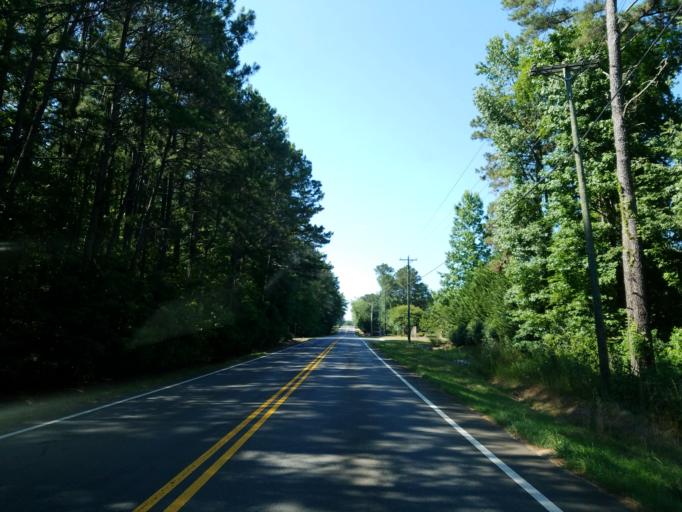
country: US
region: Georgia
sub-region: Fulton County
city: Milton
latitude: 34.2090
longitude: -84.2894
